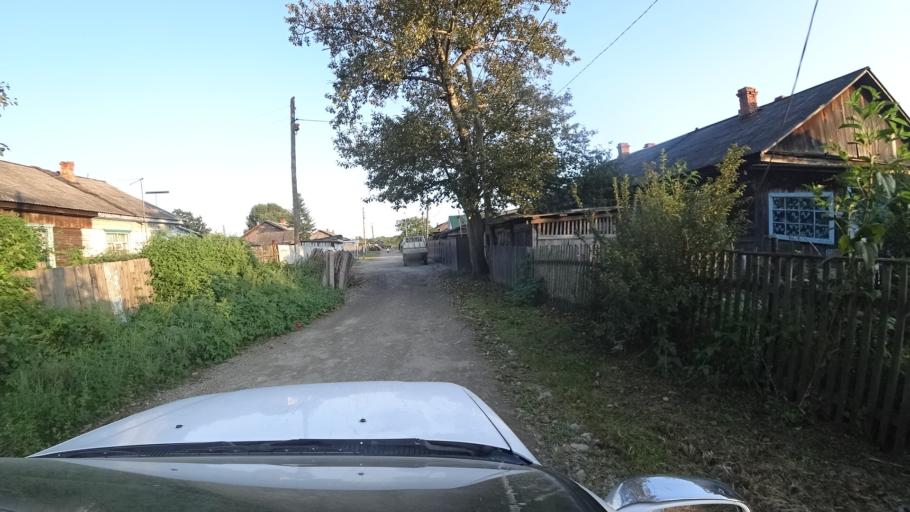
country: RU
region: Primorskiy
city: Dal'nerechensk
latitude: 45.9417
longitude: 133.7563
